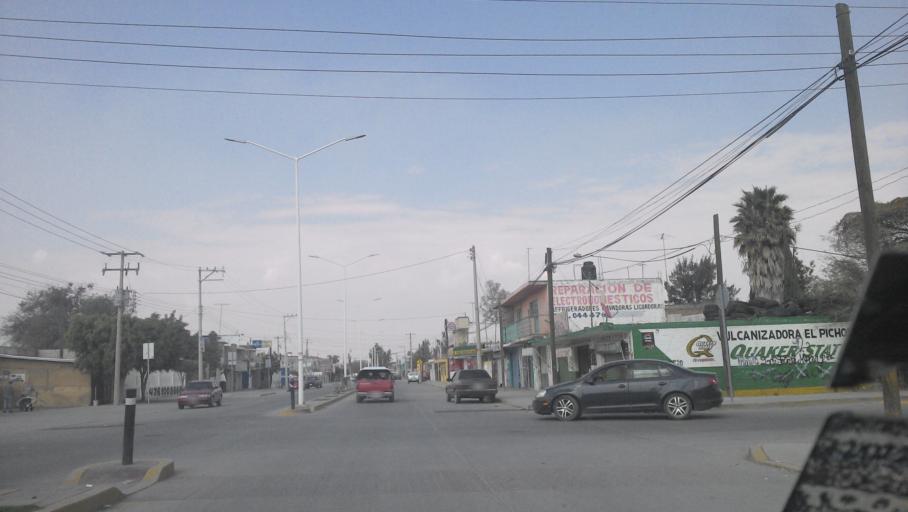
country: MX
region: Guanajuato
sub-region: San Francisco del Rincon
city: Fraccionamiento Villa Jardin
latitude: 21.0052
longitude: -101.8517
